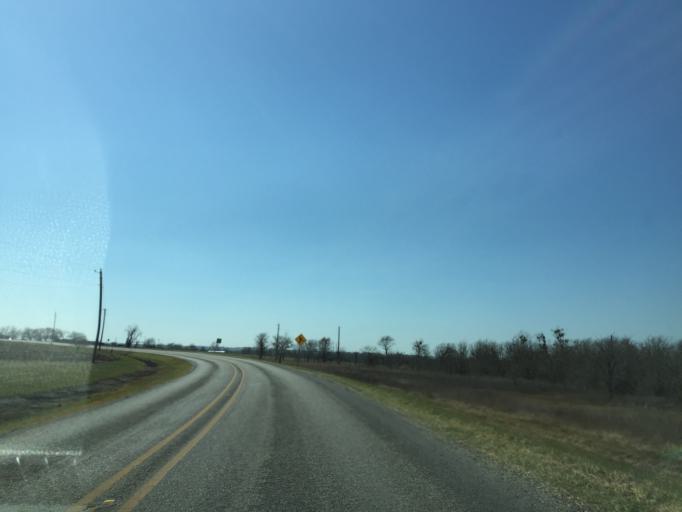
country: US
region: Texas
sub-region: Williamson County
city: Georgetown
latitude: 30.6857
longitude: -97.5890
